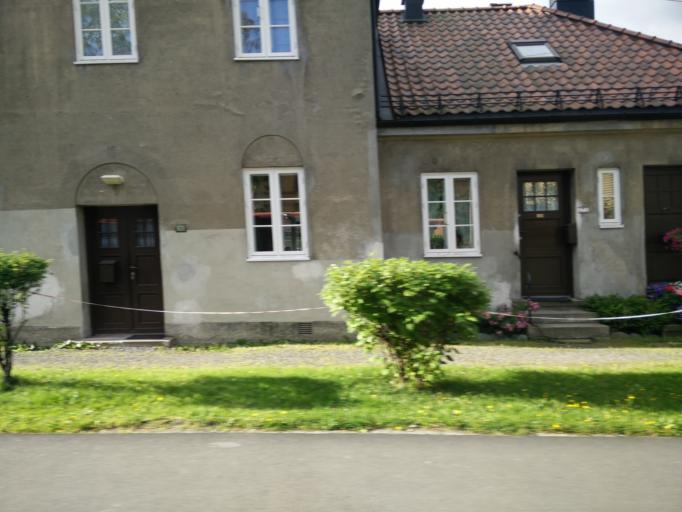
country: NO
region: Oslo
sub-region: Oslo
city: Oslo
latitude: 59.9357
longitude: 10.7371
